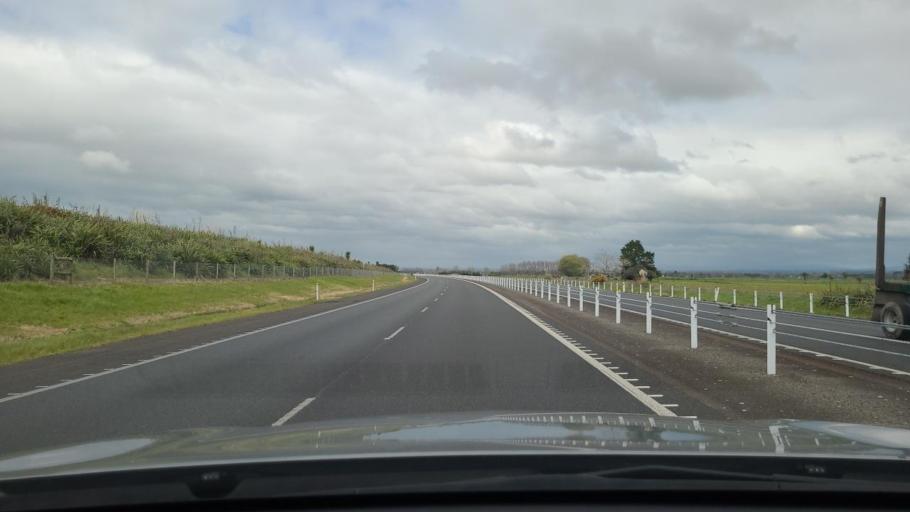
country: NZ
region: Bay of Plenty
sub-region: Western Bay of Plenty District
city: Maketu
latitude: -37.7524
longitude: 176.3594
